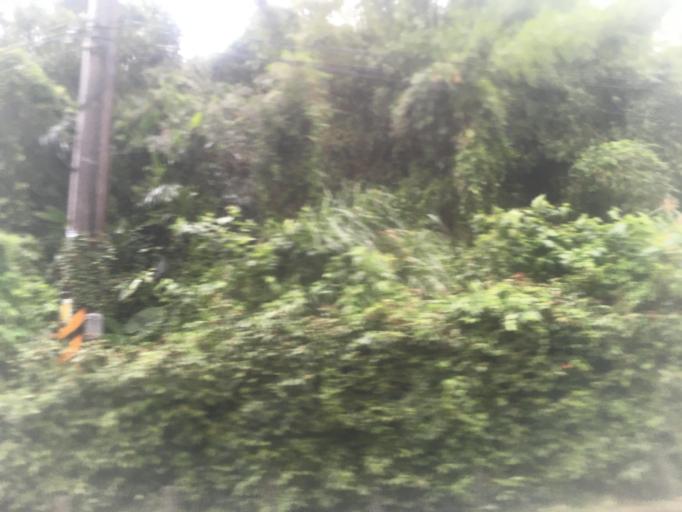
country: TW
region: Taiwan
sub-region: Keelung
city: Keelung
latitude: 25.0544
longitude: 121.9207
